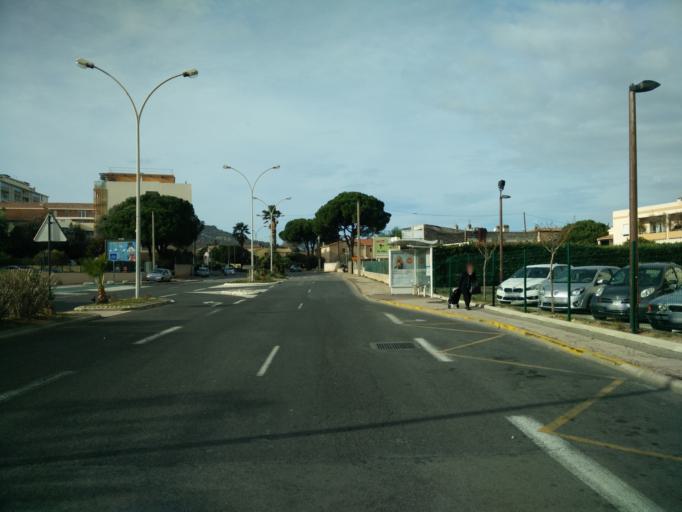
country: FR
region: Provence-Alpes-Cote d'Azur
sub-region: Departement du Var
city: Six-Fours-les-Plages
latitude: 43.1076
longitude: 5.8625
